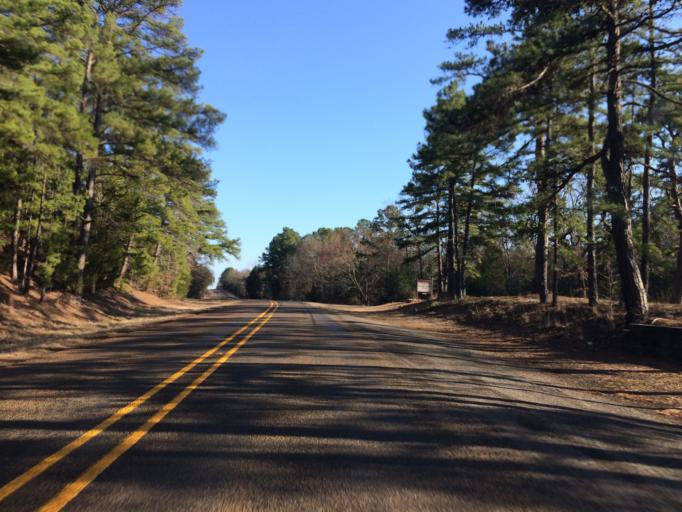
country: US
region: Texas
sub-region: Wood County
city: Hawkins
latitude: 32.6697
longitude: -95.3238
